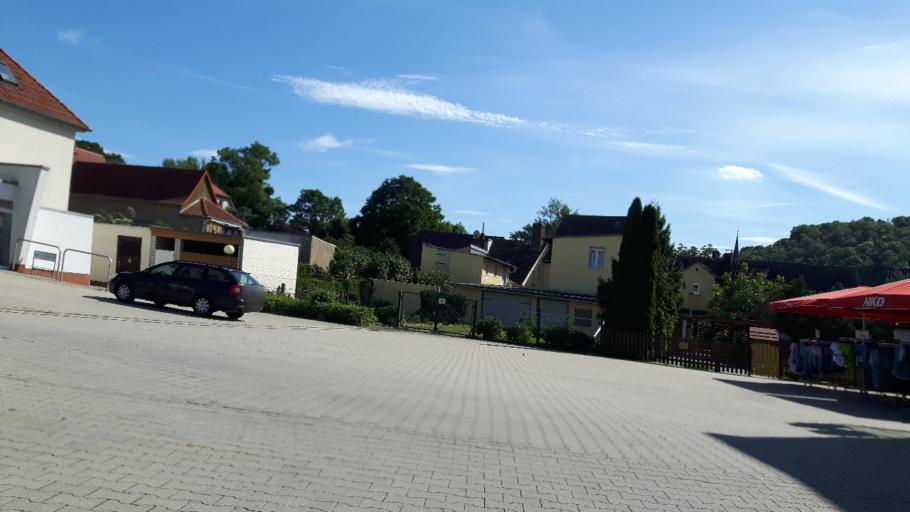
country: DE
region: Saxony-Anhalt
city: Bad Kosen
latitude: 51.1378
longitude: 11.7205
